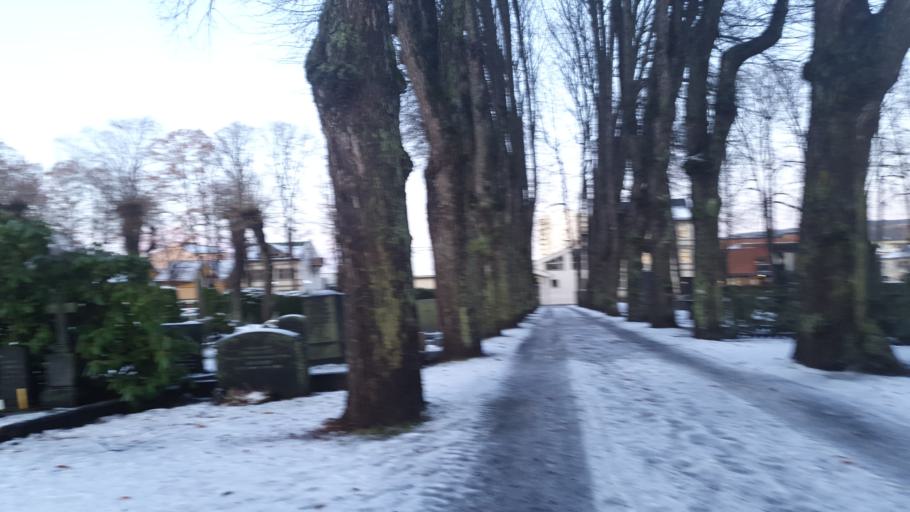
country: NO
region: Buskerud
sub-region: Drammen
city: Drammen
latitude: 59.7355
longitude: 10.2084
